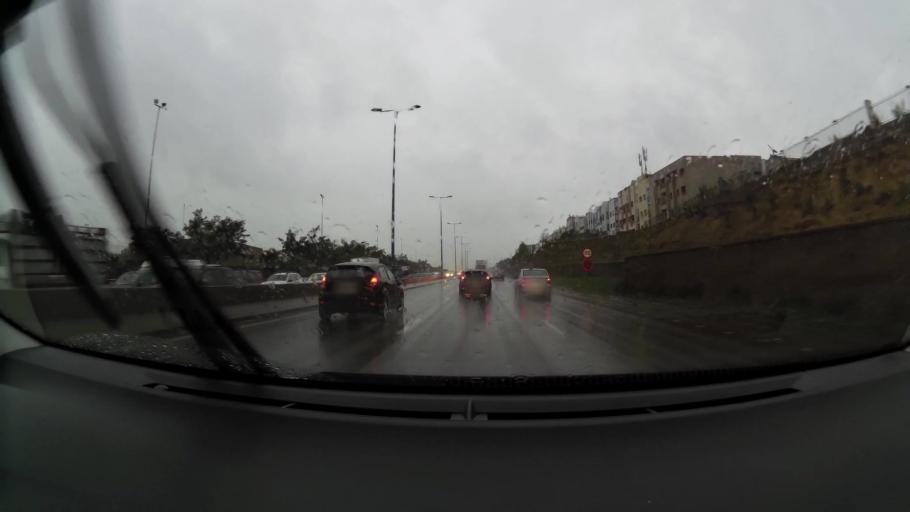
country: MA
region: Grand Casablanca
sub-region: Casablanca
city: Casablanca
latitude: 33.5815
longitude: -7.5504
